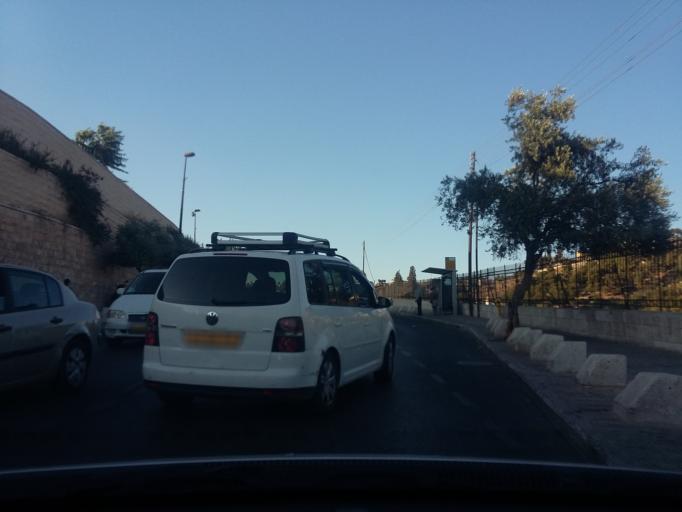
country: PS
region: West Bank
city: East Jerusalem
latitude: 31.7812
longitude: 35.2388
